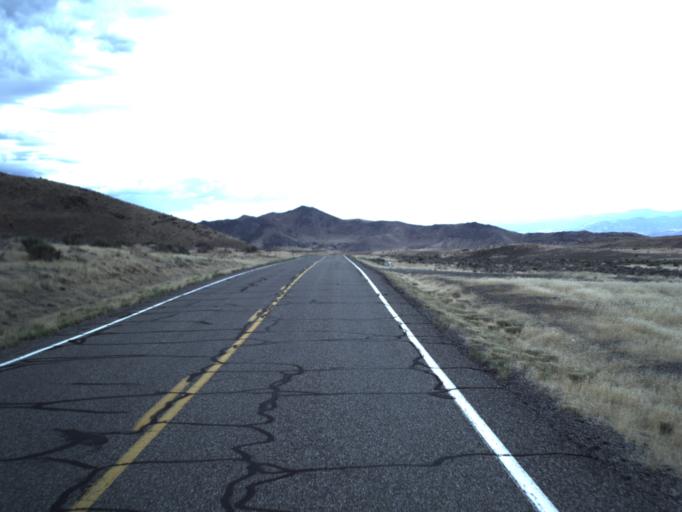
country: US
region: Utah
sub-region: Sevier County
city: Richfield
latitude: 38.7726
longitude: -111.9598
